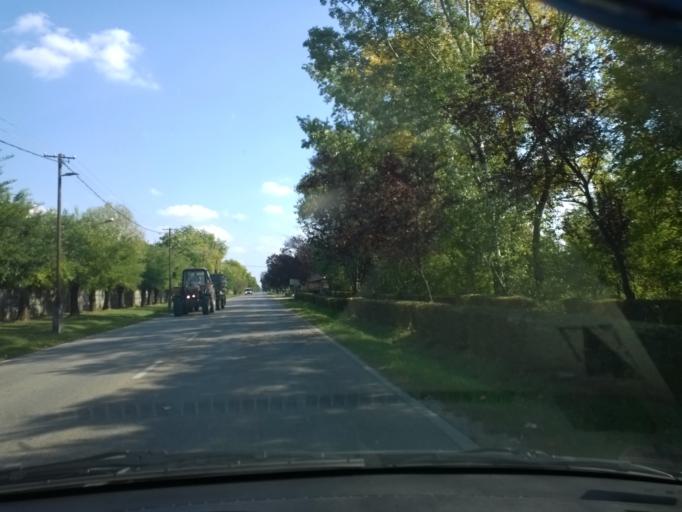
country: HU
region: Bacs-Kiskun
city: Kalocsa
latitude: 46.5199
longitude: 18.9888
